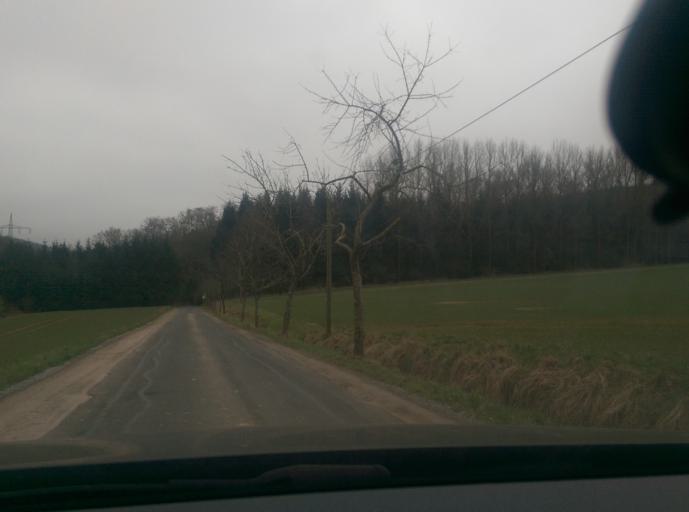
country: DE
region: Lower Saxony
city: Hameln
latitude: 52.1274
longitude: 9.3907
